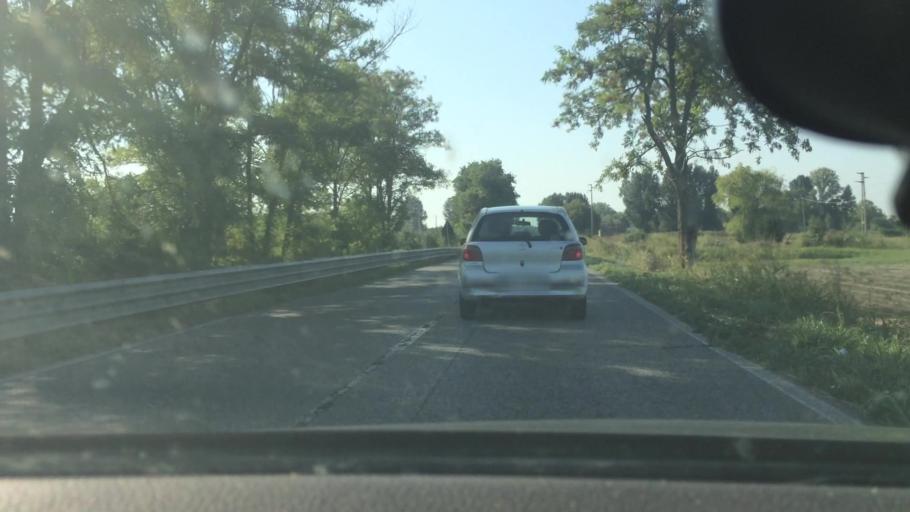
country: IT
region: Emilia-Romagna
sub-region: Provincia di Ferrara
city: Comacchio
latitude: 44.7070
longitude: 12.1631
